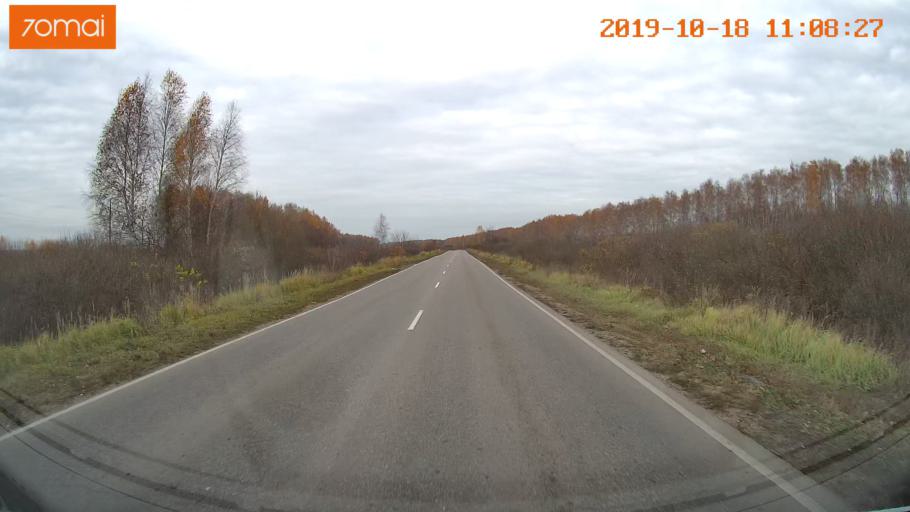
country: RU
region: Tula
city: Kimovsk
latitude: 53.9382
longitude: 38.5372
